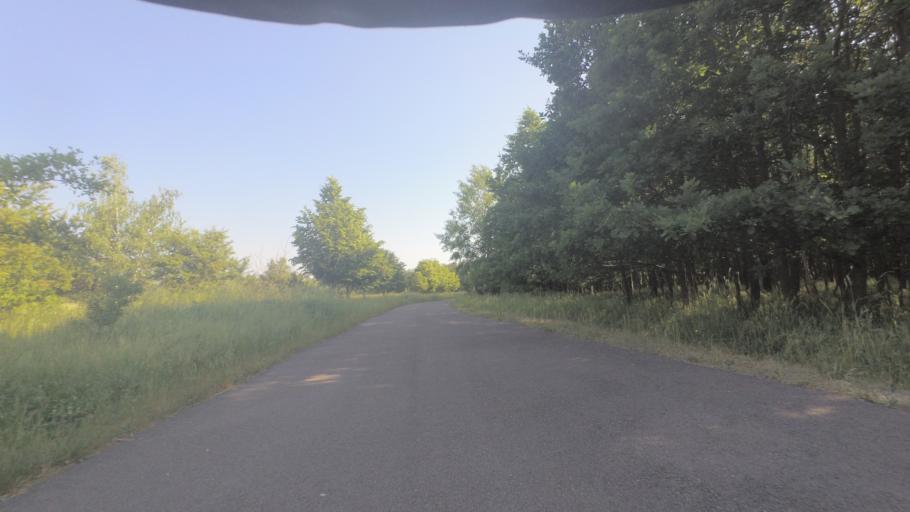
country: DE
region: Saxony-Anhalt
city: Rodleben
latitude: 51.8374
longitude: 12.1658
